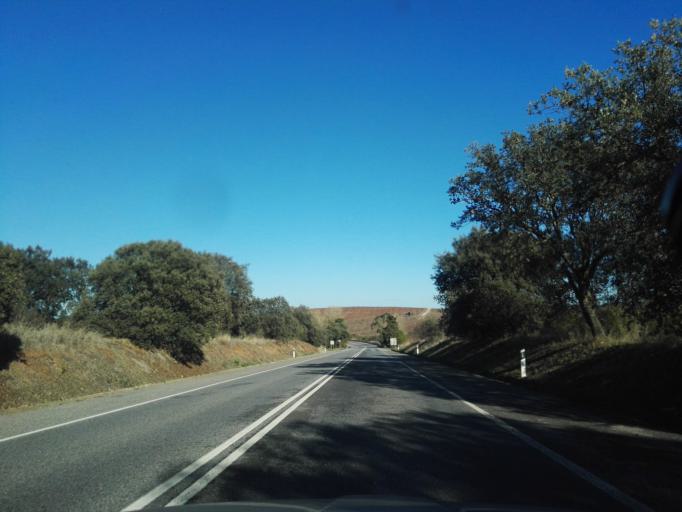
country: PT
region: Evora
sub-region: Vila Vicosa
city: Vila Vicosa
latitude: 38.8294
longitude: -7.4076
